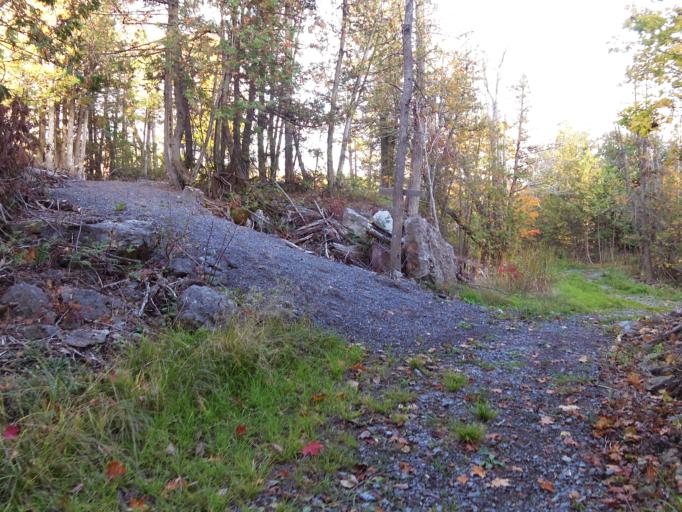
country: CA
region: Ontario
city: Pembroke
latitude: 45.5346
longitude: -77.0926
